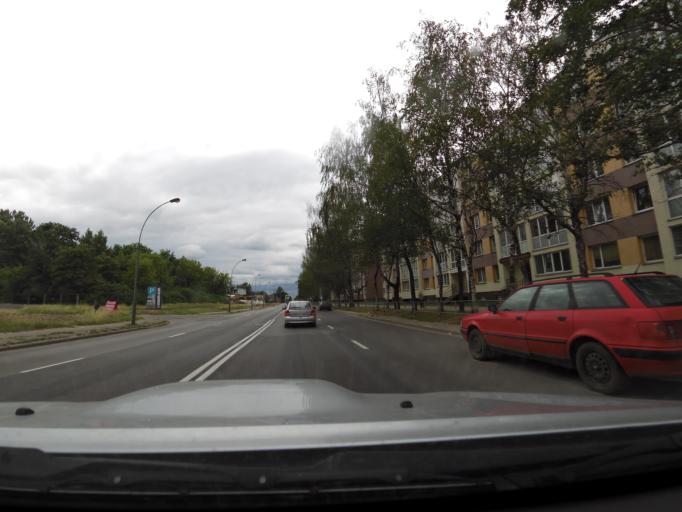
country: LT
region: Panevezys
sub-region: Panevezys City
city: Panevezys
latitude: 55.7185
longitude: 24.3750
